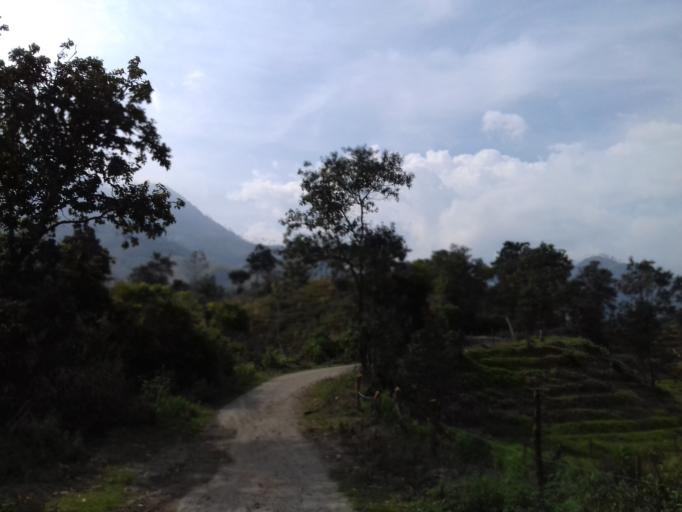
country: CO
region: Tolima
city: Cajamarca
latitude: 4.5162
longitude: -75.4045
